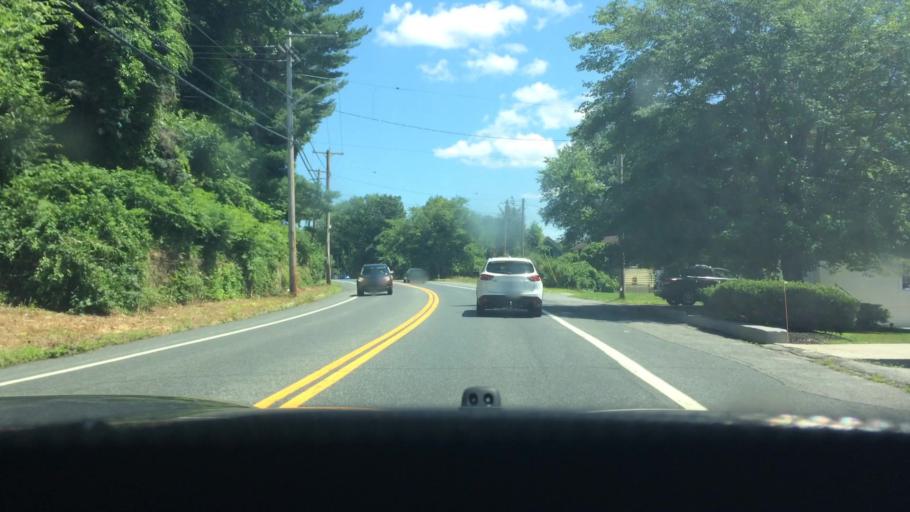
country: US
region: Massachusetts
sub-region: Worcester County
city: Blackstone
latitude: 41.9981
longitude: -71.5476
